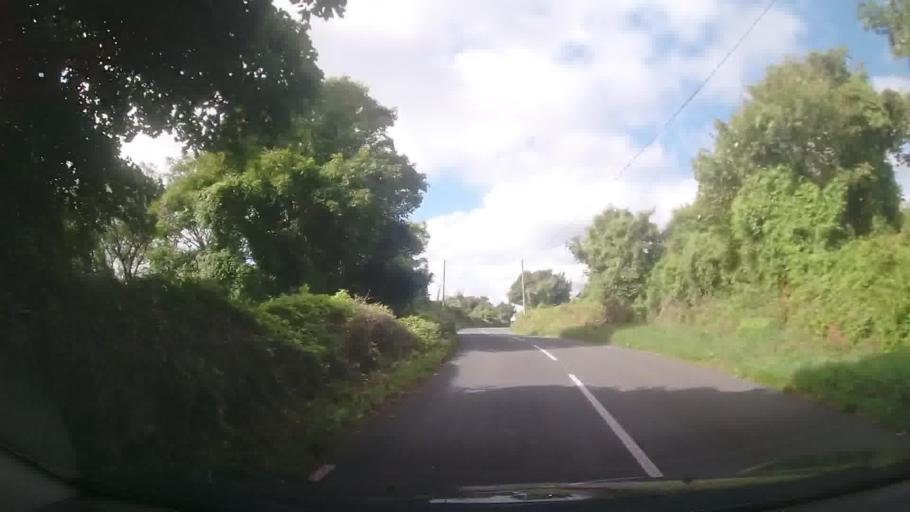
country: GB
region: Wales
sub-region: Pembrokeshire
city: Manorbier
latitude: 51.6540
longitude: -4.7624
